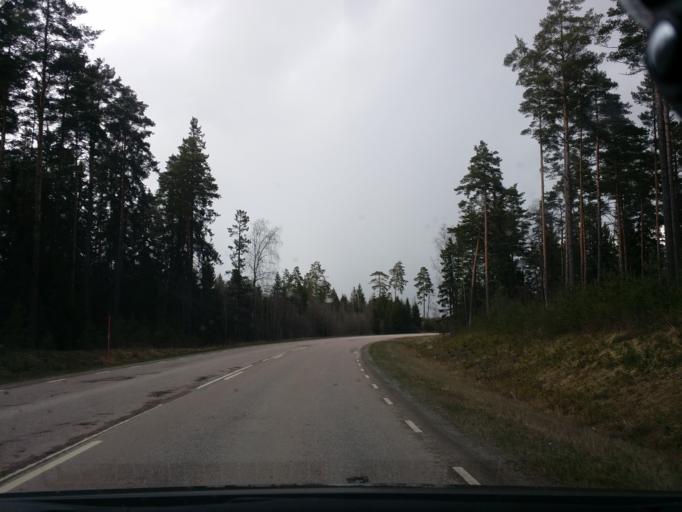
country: SE
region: Uppsala
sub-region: Enkopings Kommun
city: Enkoping
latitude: 59.6270
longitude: 17.1356
